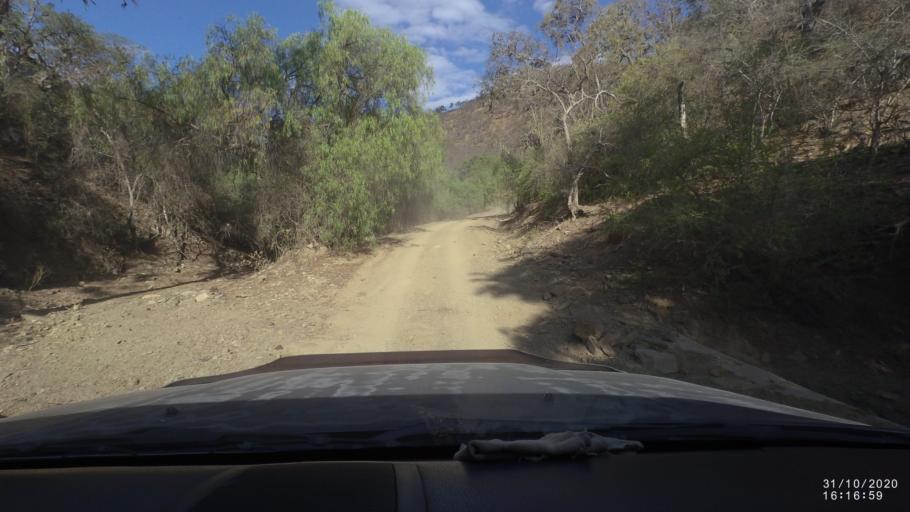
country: BO
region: Chuquisaca
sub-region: Provincia Zudanez
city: Mojocoya
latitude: -18.3906
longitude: -64.6061
